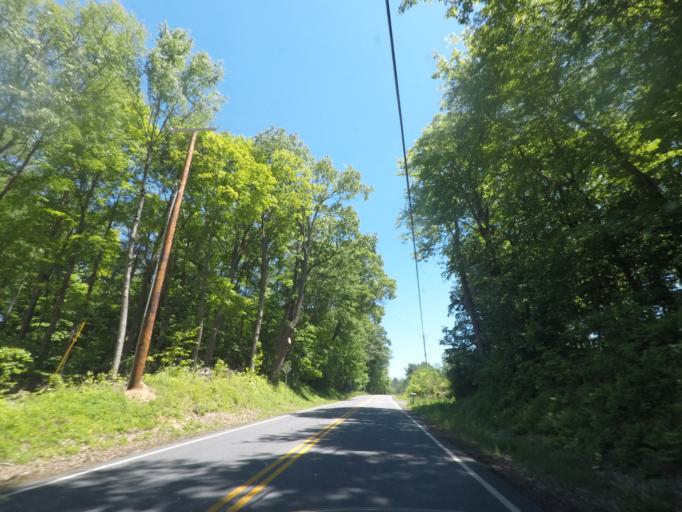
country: US
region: New York
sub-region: Saratoga County
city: Country Knolls
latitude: 42.9440
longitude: -73.7598
